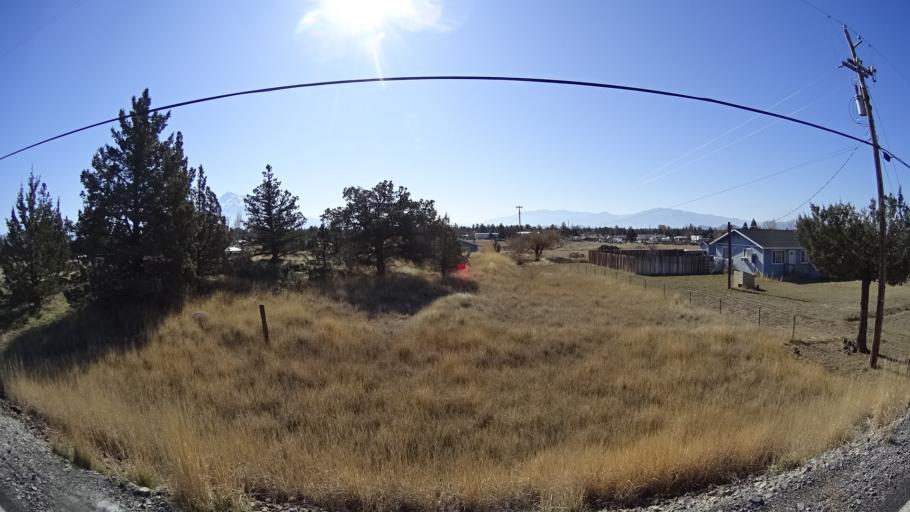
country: US
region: California
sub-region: Siskiyou County
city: Montague
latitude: 41.6599
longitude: -122.3926
